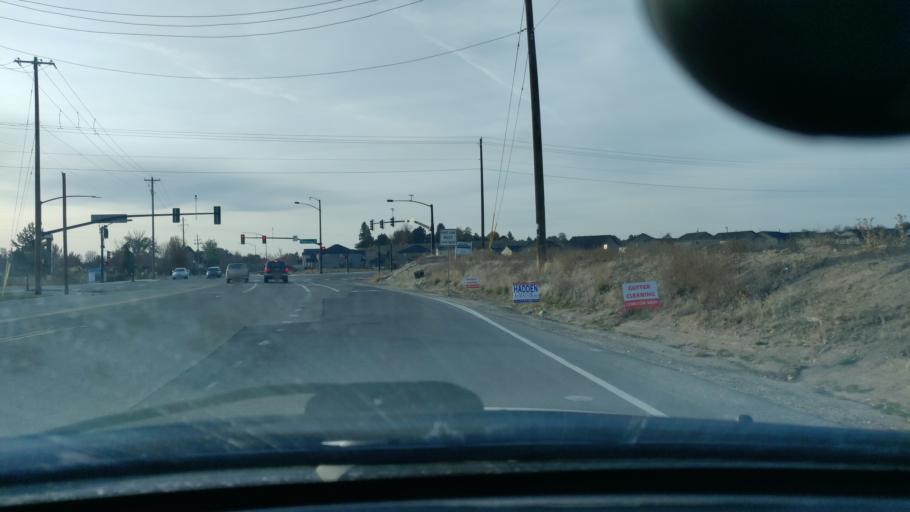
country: US
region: Idaho
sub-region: Ada County
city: Eagle
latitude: 43.6934
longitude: -116.3181
